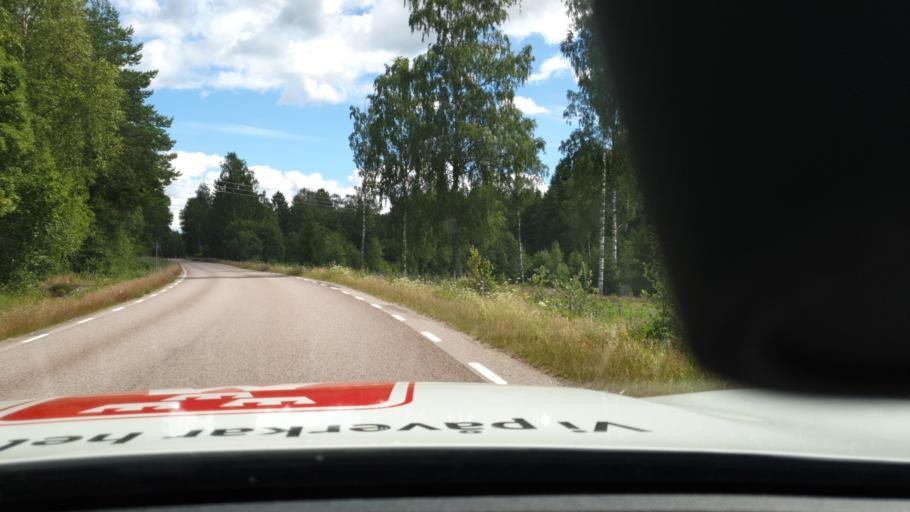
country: SE
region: Vaermland
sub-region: Kristinehamns Kommun
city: Kristinehamn
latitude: 59.3298
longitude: 14.1741
